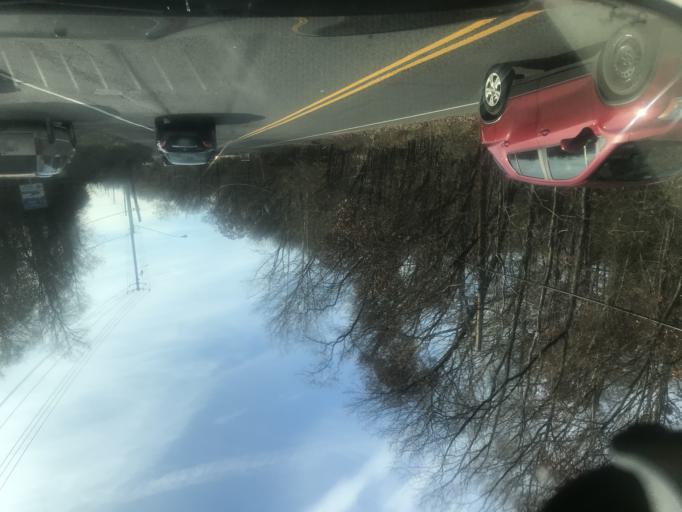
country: US
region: Maryland
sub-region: Prince George's County
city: Forest Heights
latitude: 38.8140
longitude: -76.9946
